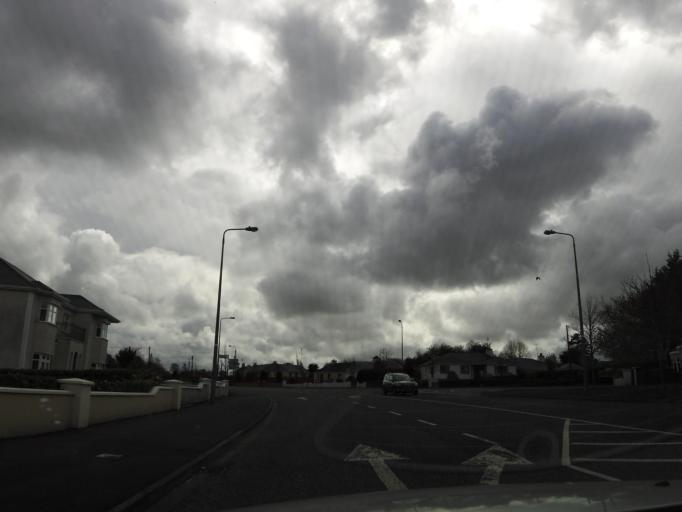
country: IE
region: Connaught
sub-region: Maigh Eo
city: Claremorris
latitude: 53.7154
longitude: -9.0046
